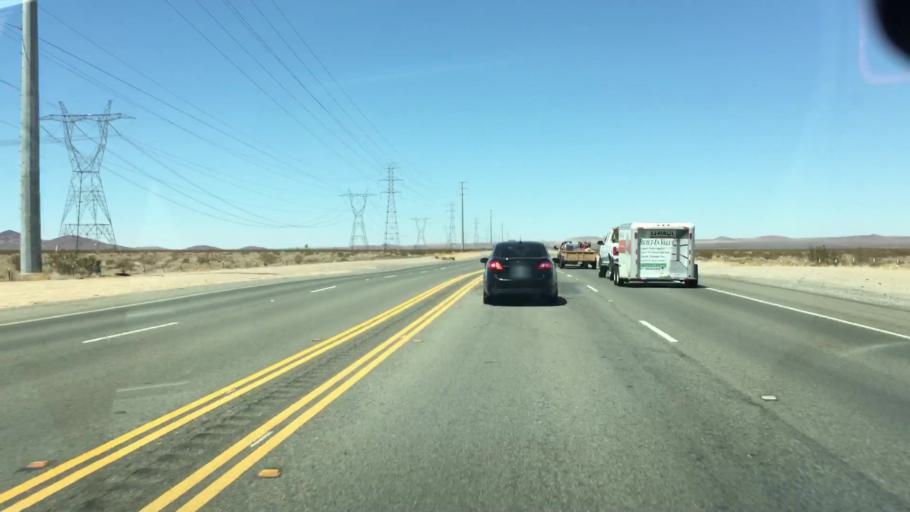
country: US
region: California
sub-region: San Bernardino County
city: Adelanto
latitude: 34.7674
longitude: -117.4762
